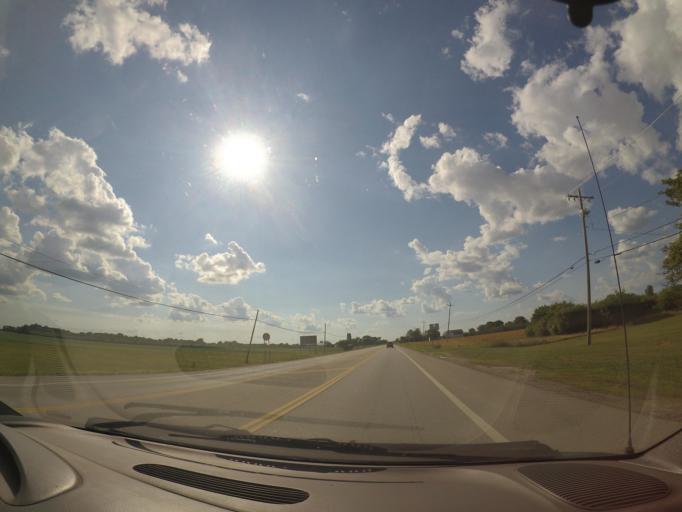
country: US
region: Ohio
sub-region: Wood County
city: Perrysburg
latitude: 41.5359
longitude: -83.5689
